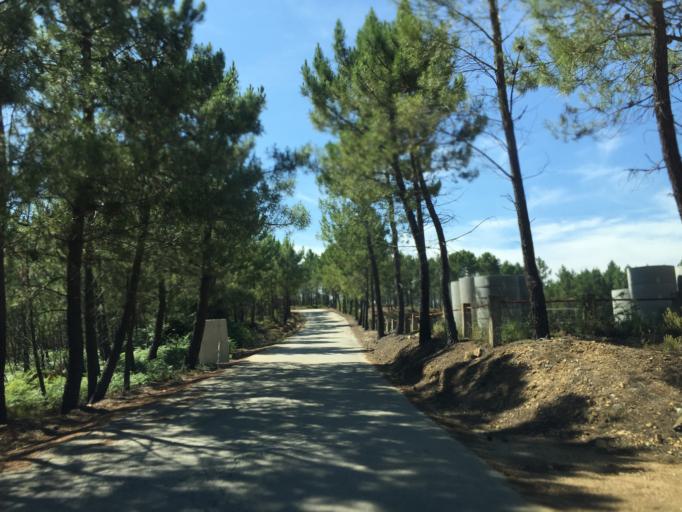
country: PT
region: Castelo Branco
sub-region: Oleiros
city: Oleiros
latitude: 39.9774
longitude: -7.8434
